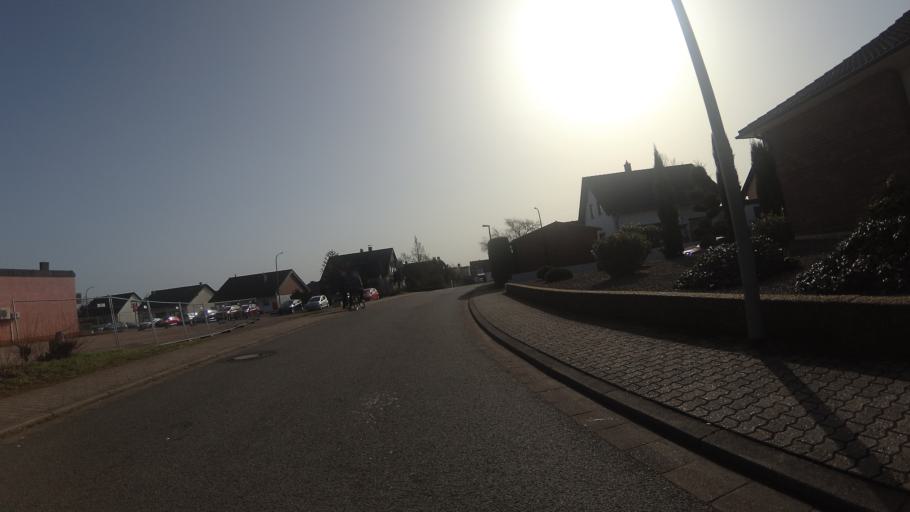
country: DE
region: Saarland
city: Uberherrn
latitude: 49.2729
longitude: 6.7072
